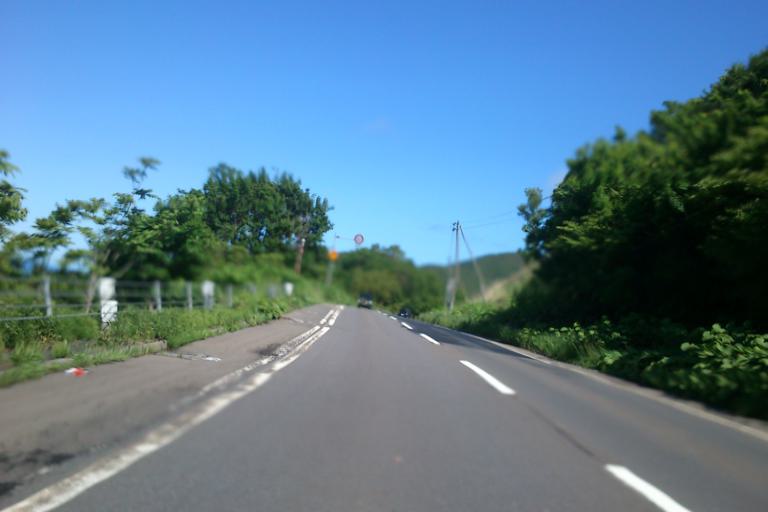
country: JP
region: Hokkaido
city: Ishikari
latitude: 43.5029
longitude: 141.3743
